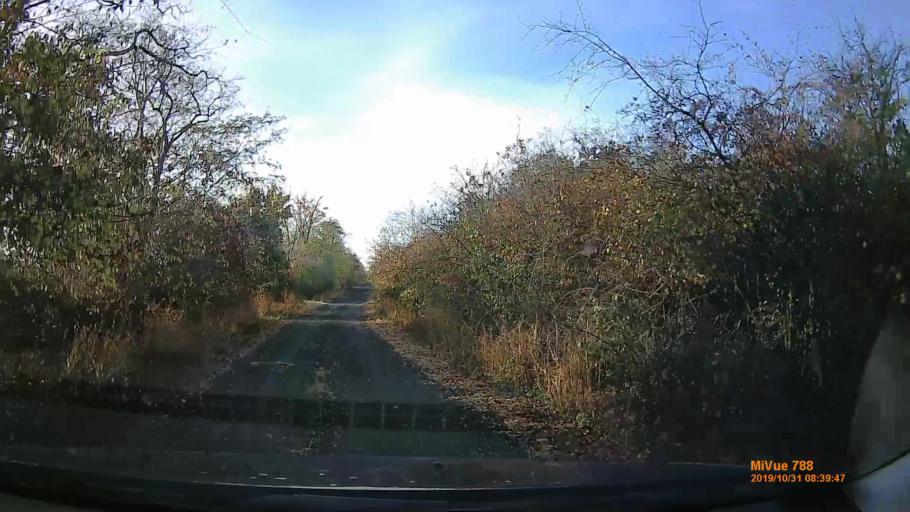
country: HU
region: Pest
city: Pand
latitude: 47.3100
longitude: 19.6486
